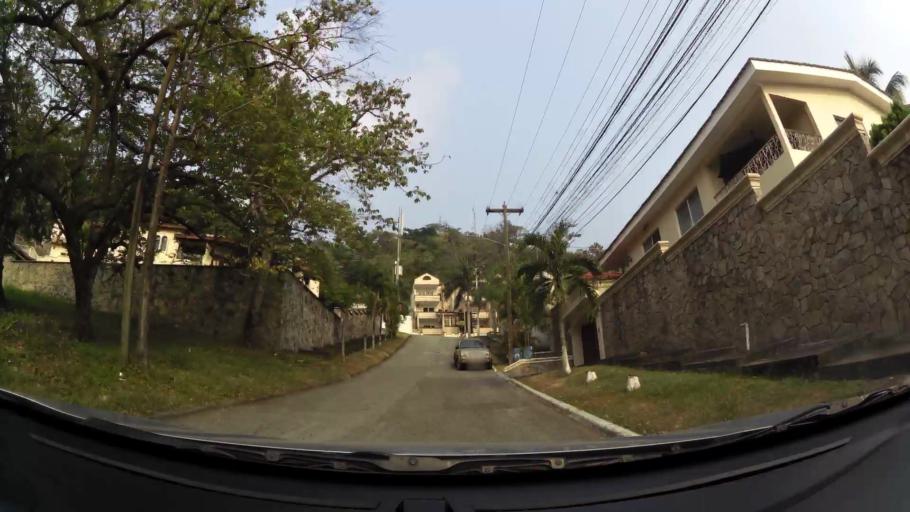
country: HN
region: Cortes
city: Armenta
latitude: 15.4982
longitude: -88.0506
